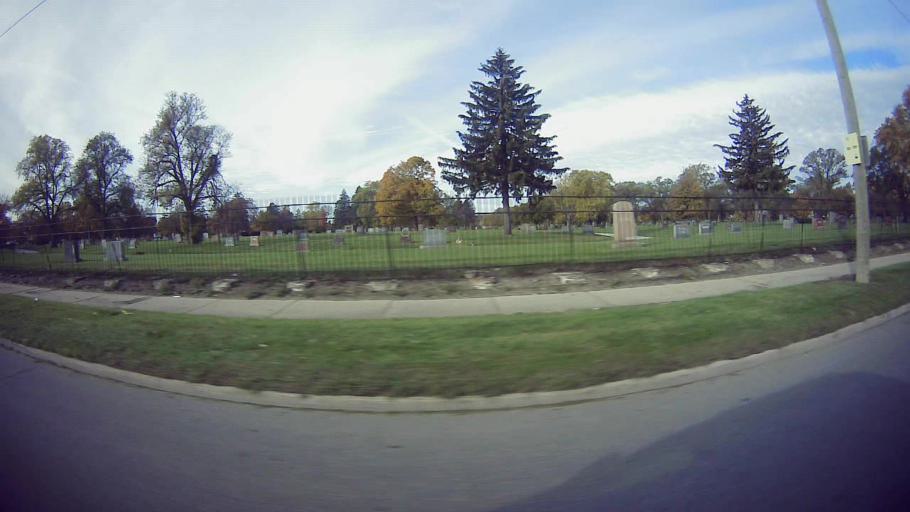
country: US
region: Michigan
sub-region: Wayne County
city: Hamtramck
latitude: 42.4115
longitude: -83.0235
